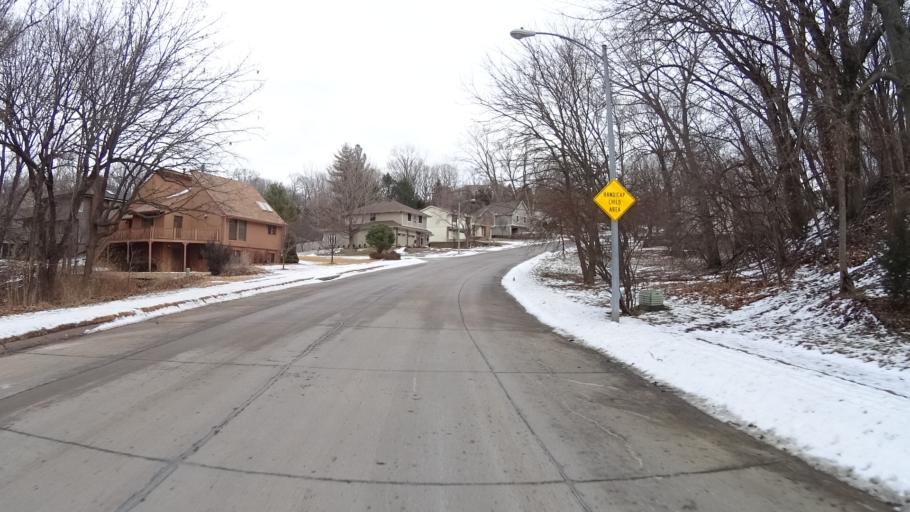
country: US
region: Nebraska
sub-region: Sarpy County
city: Bellevue
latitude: 41.1754
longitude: -95.9141
